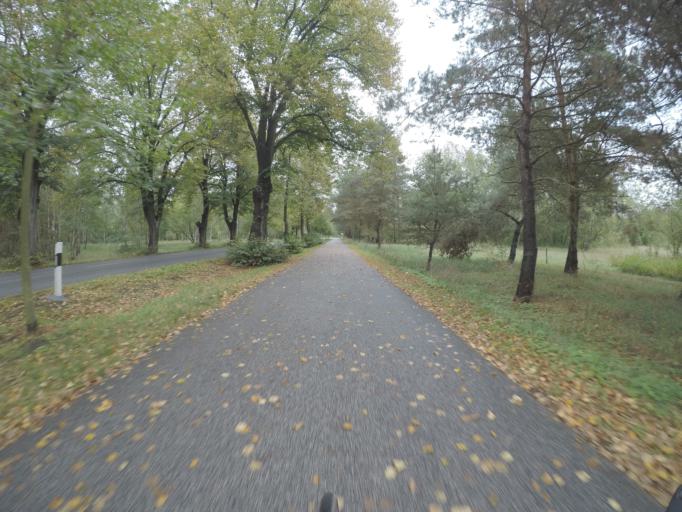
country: DE
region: Berlin
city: Buch
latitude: 52.6718
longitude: 13.4983
